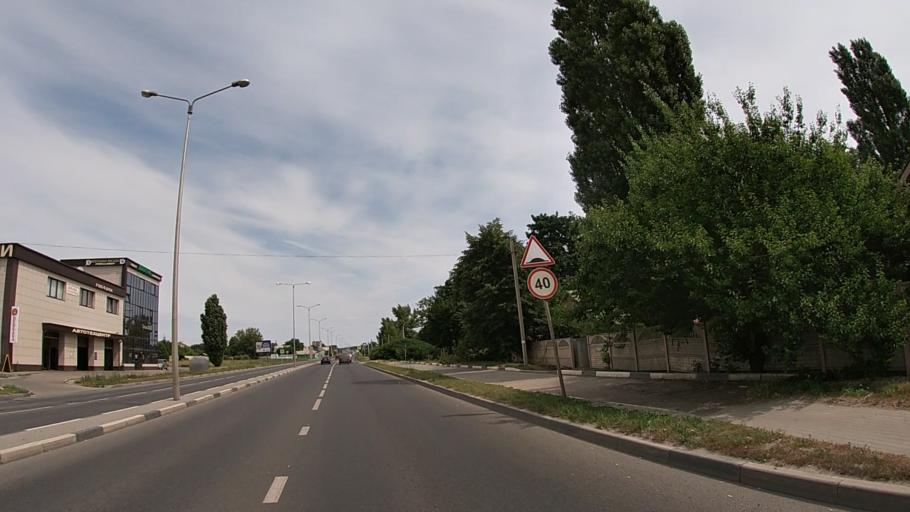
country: RU
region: Belgorod
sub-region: Belgorodskiy Rayon
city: Belgorod
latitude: 50.6179
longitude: 36.5393
